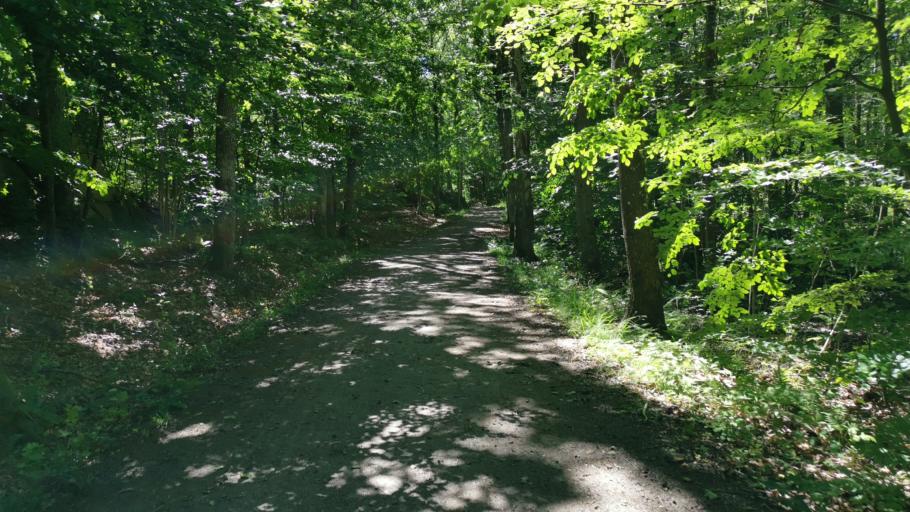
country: SE
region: Vaestra Goetaland
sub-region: Lysekils Kommun
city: Lysekil
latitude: 58.2416
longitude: 11.4851
